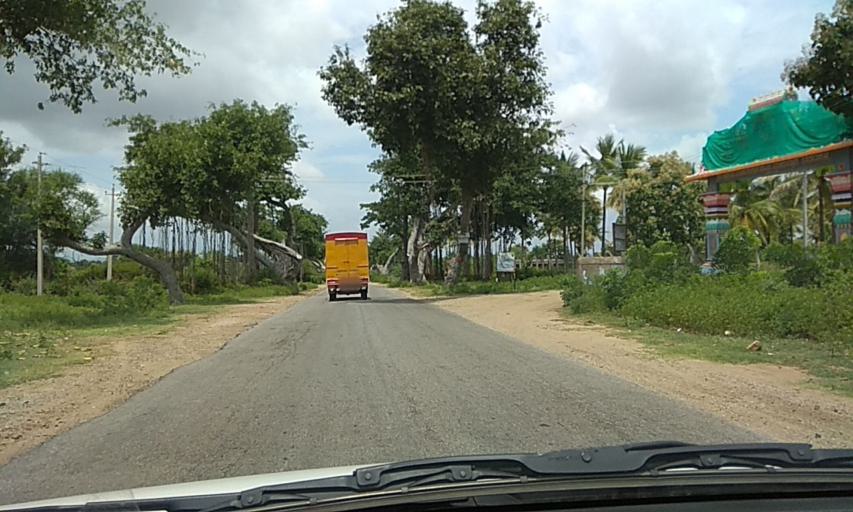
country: IN
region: Karnataka
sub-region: Chamrajnagar
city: Gundlupet
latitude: 11.8122
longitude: 76.7703
